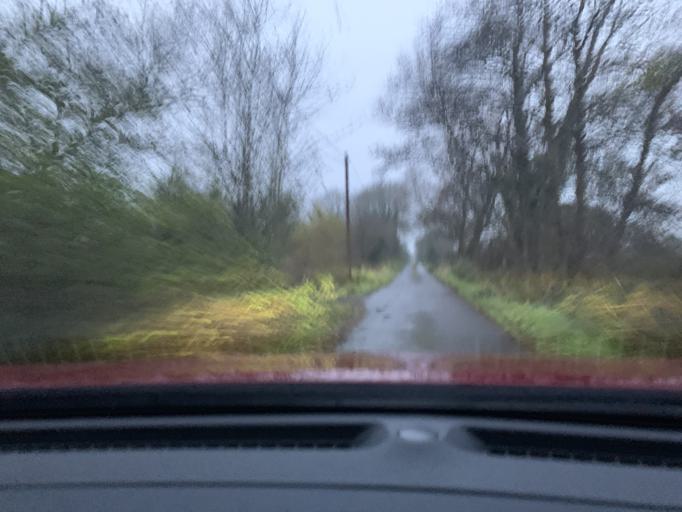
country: IE
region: Connaught
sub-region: Sligo
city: Ballymote
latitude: 54.0184
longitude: -8.5269
